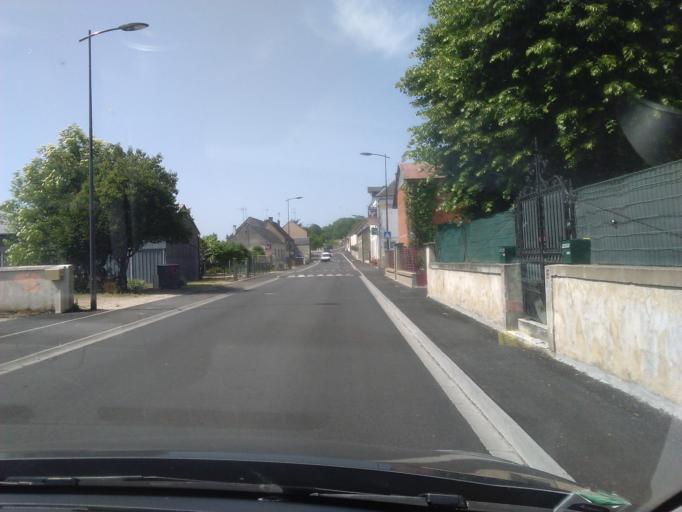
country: FR
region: Centre
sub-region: Departement du Loir-et-Cher
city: Naveil
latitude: 47.7972
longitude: 1.0230
